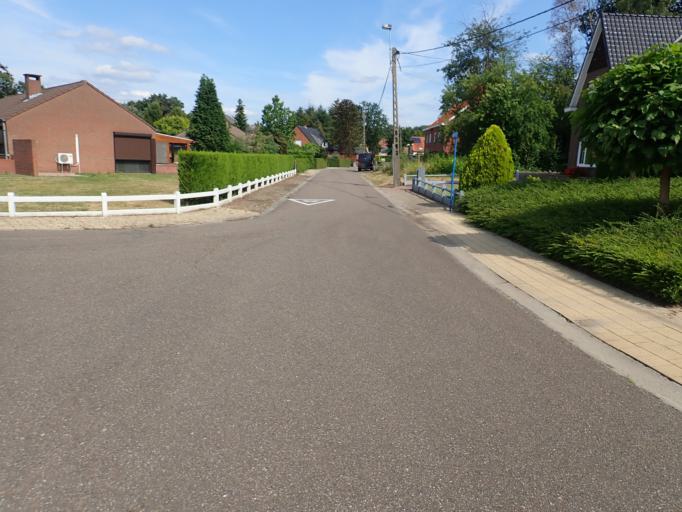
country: BE
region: Flanders
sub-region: Provincie Vlaams-Brabant
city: Keerbergen
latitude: 50.9985
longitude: 4.6319
